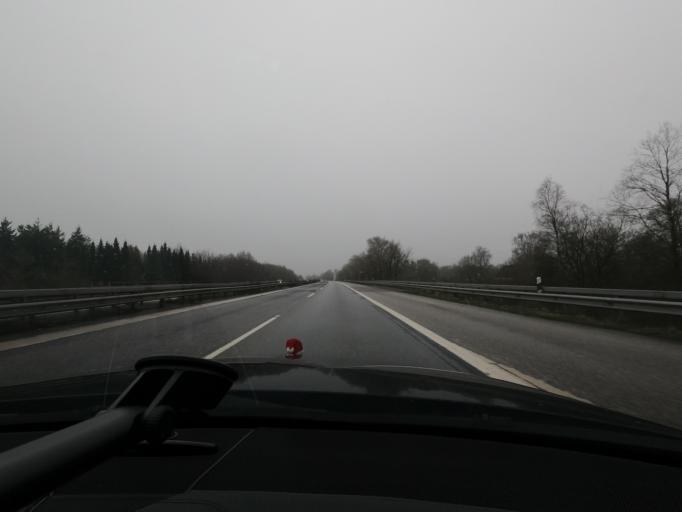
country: DE
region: Schleswig-Holstein
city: Lottorf
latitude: 54.4287
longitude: 9.5977
